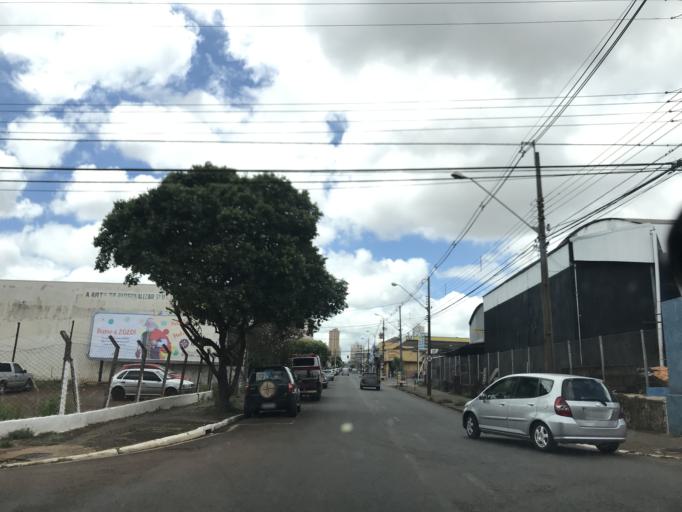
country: BR
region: Parana
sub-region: Londrina
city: Londrina
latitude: -23.2981
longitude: -51.1628
